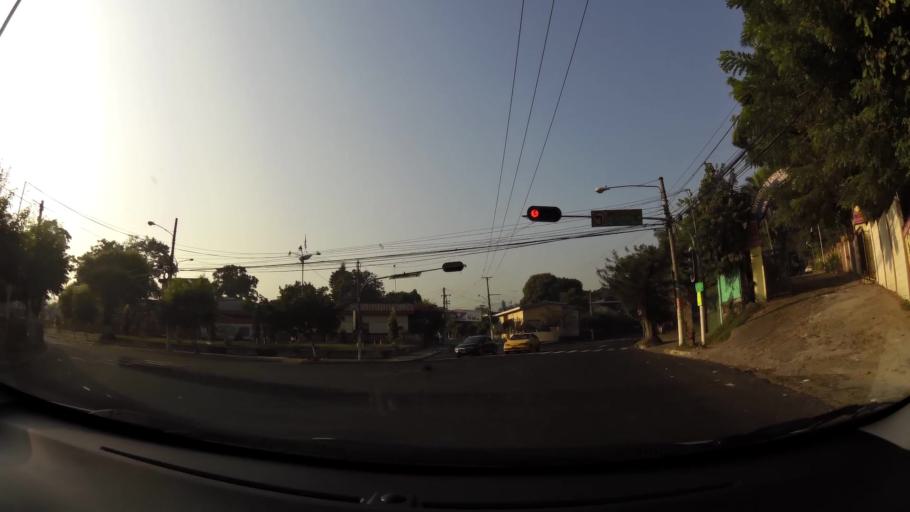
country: SV
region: San Salvador
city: San Salvador
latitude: 13.6836
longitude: -89.1968
